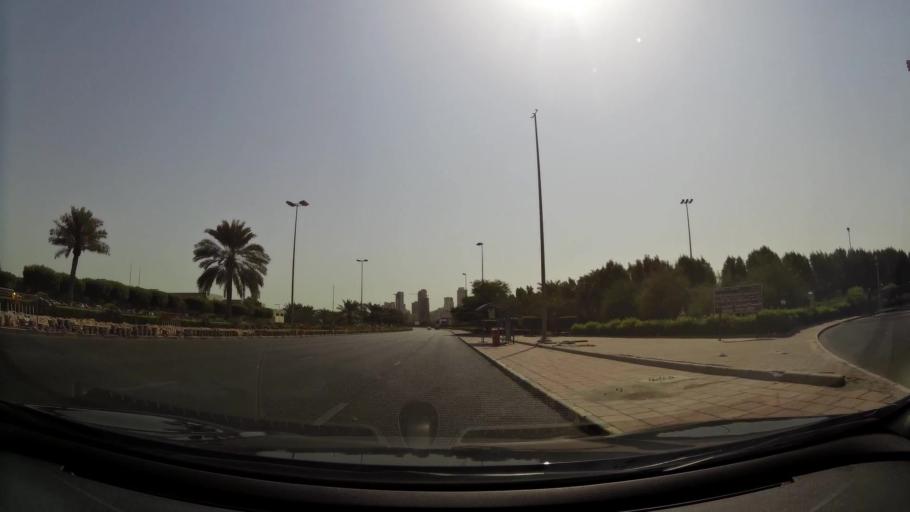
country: KW
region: Al Asimah
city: Ad Dasmah
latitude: 29.3648
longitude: 48.0220
